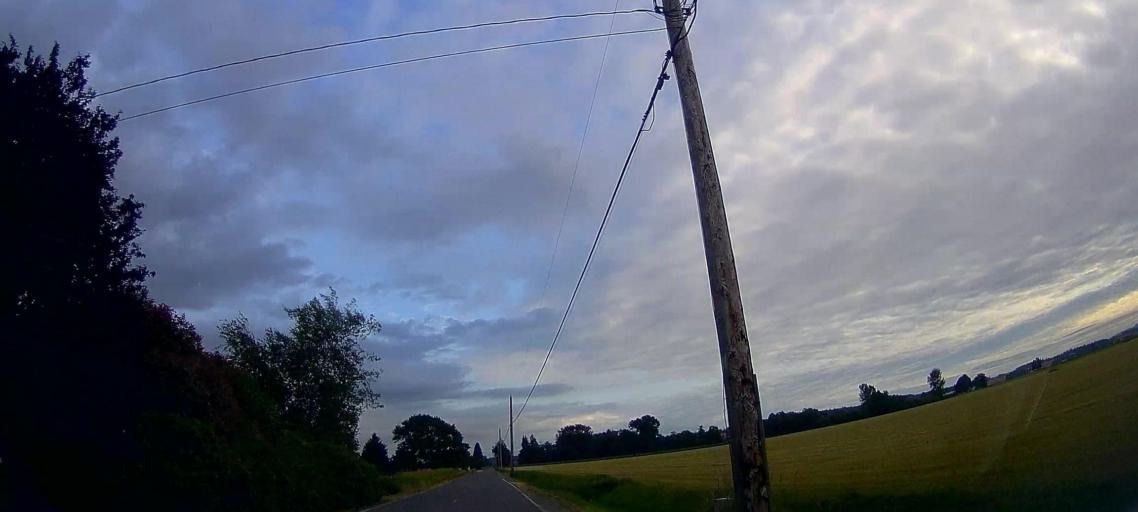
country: US
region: Washington
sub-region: Skagit County
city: Burlington
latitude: 48.5380
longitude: -122.4113
